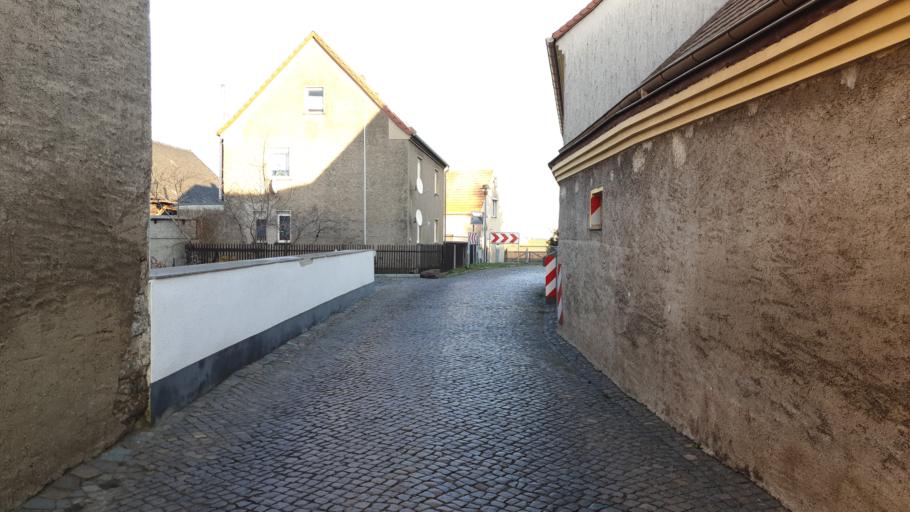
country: DE
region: Saxony
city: Mockrehna
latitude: 51.4794
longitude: 12.8519
